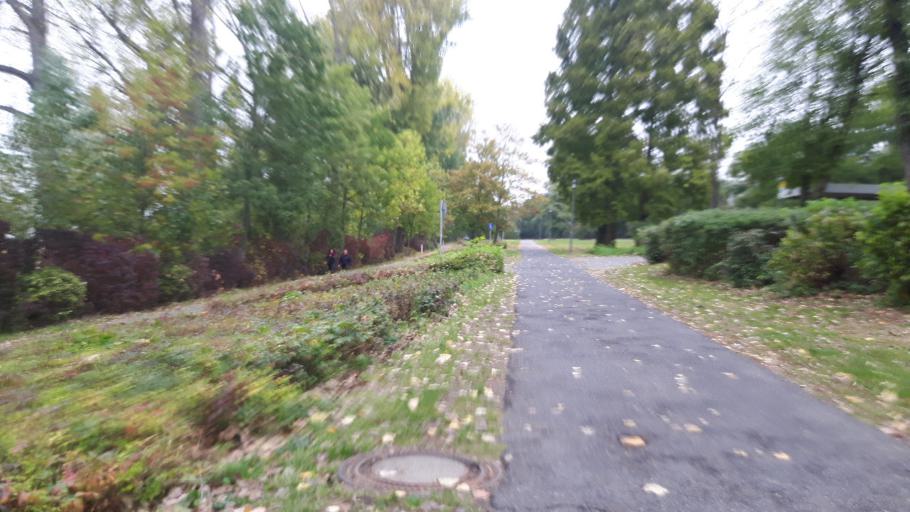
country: DE
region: North Rhine-Westphalia
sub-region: Regierungsbezirk Koln
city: Konigswinter
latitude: 50.7003
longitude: 7.1737
